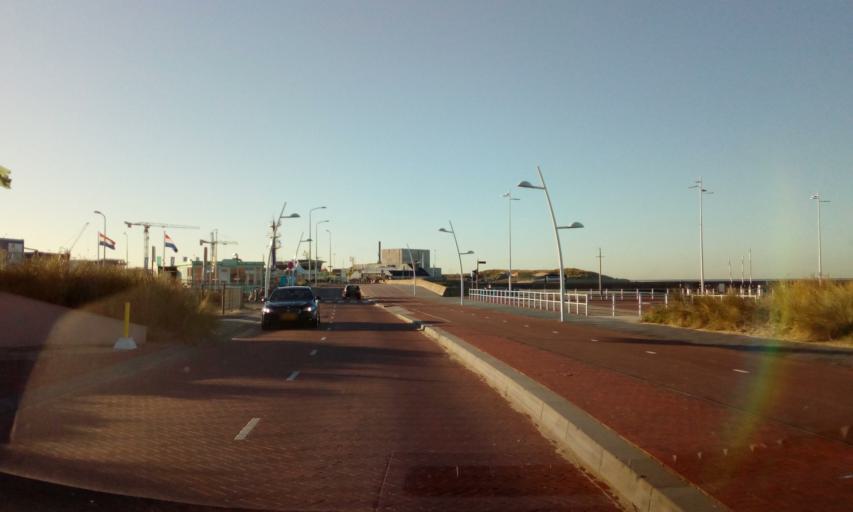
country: NL
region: South Holland
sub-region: Gemeente Den Haag
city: Scheveningen
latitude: 52.1010
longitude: 4.2626
